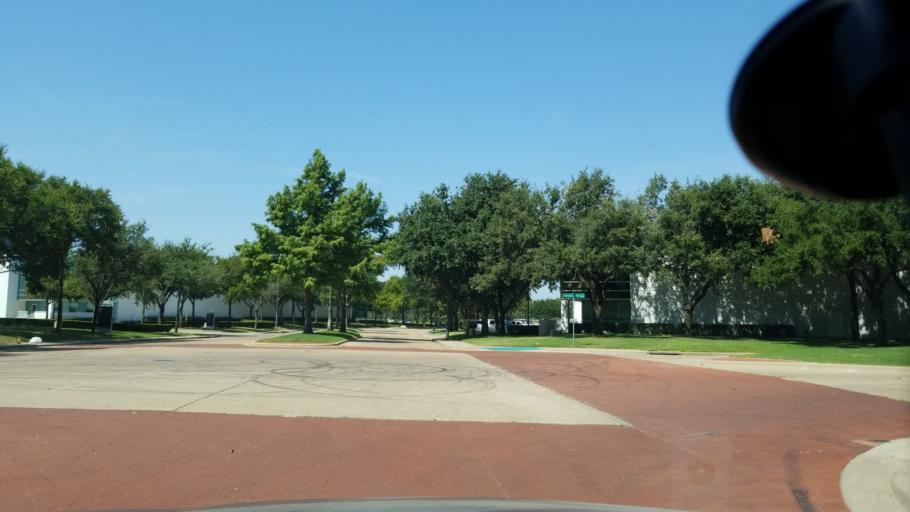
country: US
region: Texas
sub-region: Dallas County
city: Farmers Branch
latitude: 32.9040
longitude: -96.9041
